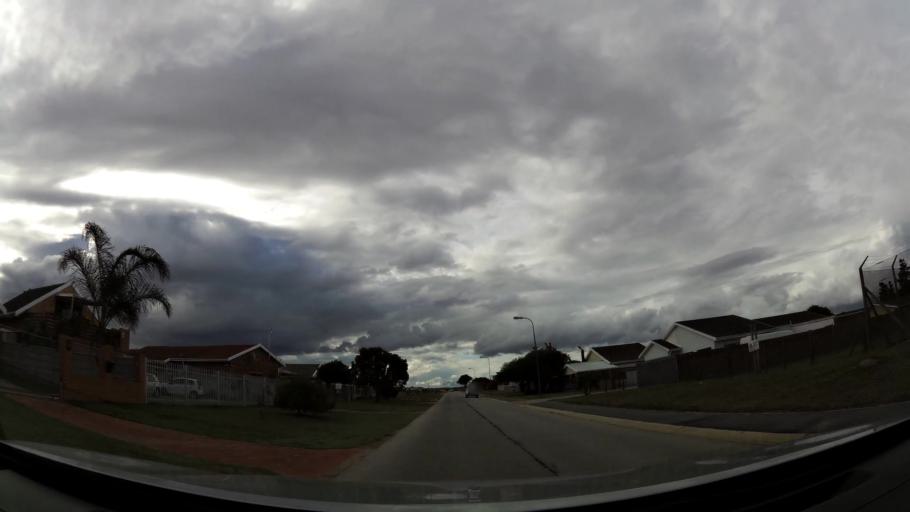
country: ZA
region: Eastern Cape
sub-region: Nelson Mandela Bay Metropolitan Municipality
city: Port Elizabeth
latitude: -33.9367
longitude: 25.4635
